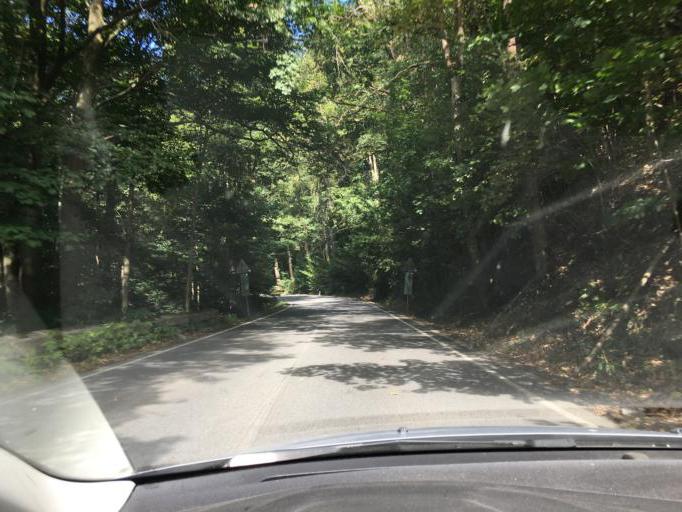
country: CZ
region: Liberecky
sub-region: Okres Semily
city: Ponikla
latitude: 50.6437
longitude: 15.4600
